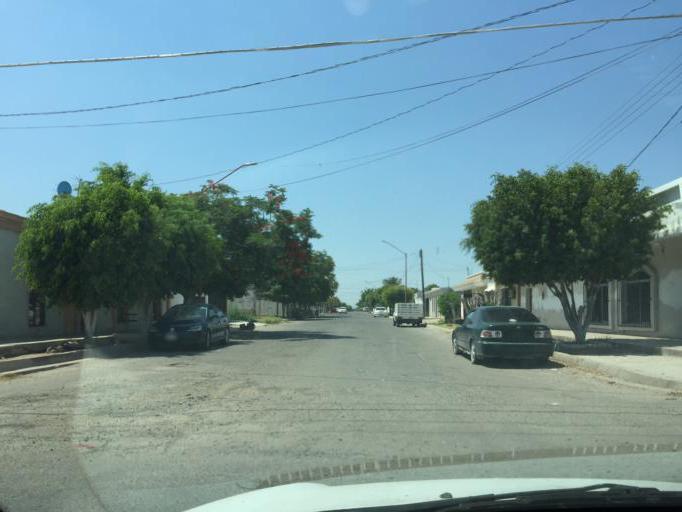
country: MX
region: Sonora
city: Navojoa
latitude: 27.0813
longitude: -109.4573
